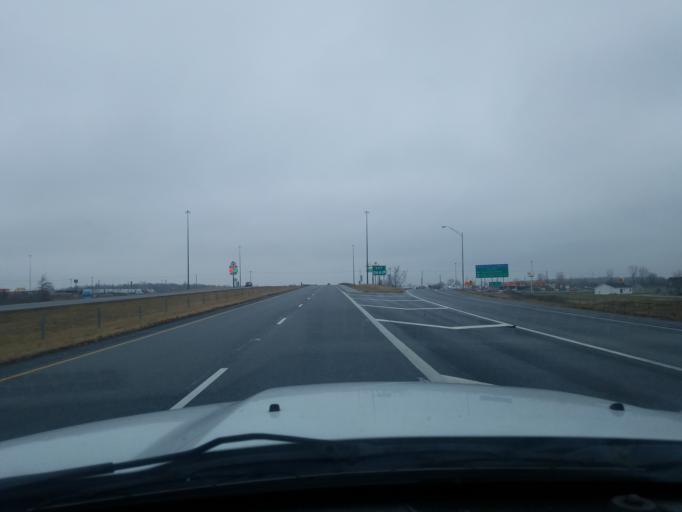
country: US
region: Indiana
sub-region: Grant County
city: Gas City
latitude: 40.5507
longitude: -85.5507
